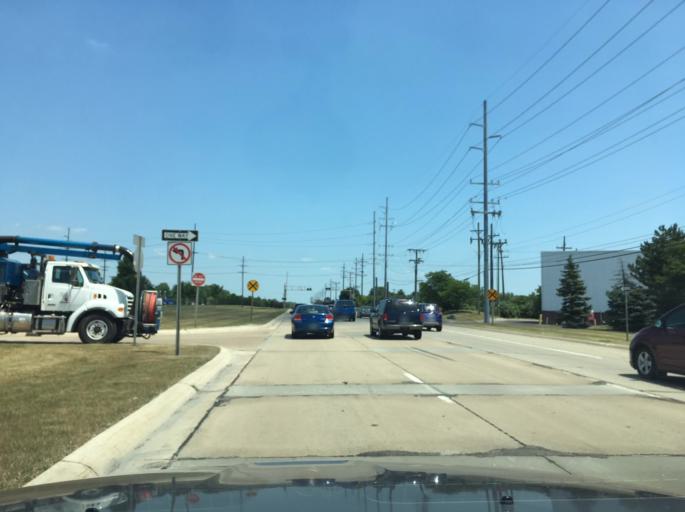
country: US
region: Michigan
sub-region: Macomb County
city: Mount Clemens
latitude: 42.6297
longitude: -82.8729
